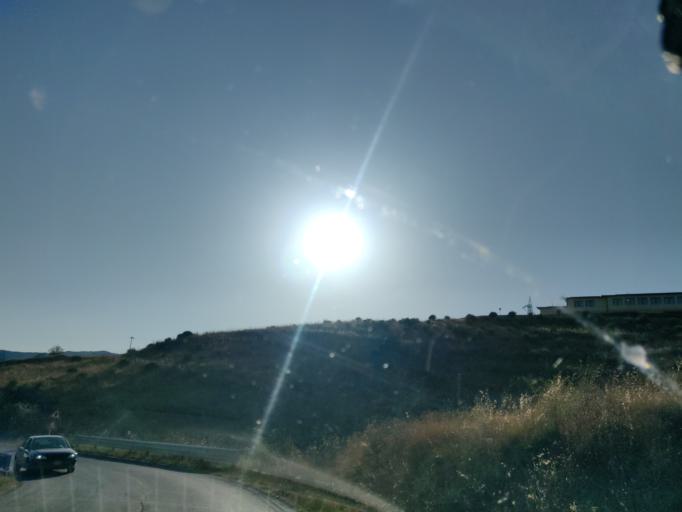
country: IT
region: Tuscany
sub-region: Provincia di Siena
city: Piancastagnaio
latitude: 42.8417
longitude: 11.7015
